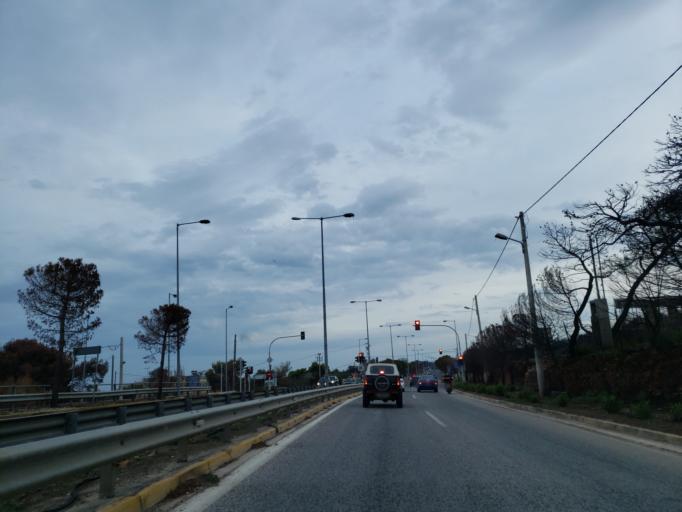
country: GR
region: Attica
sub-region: Nomarchia Anatolikis Attikis
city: Neos Voutzas
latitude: 38.0503
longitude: 23.9871
